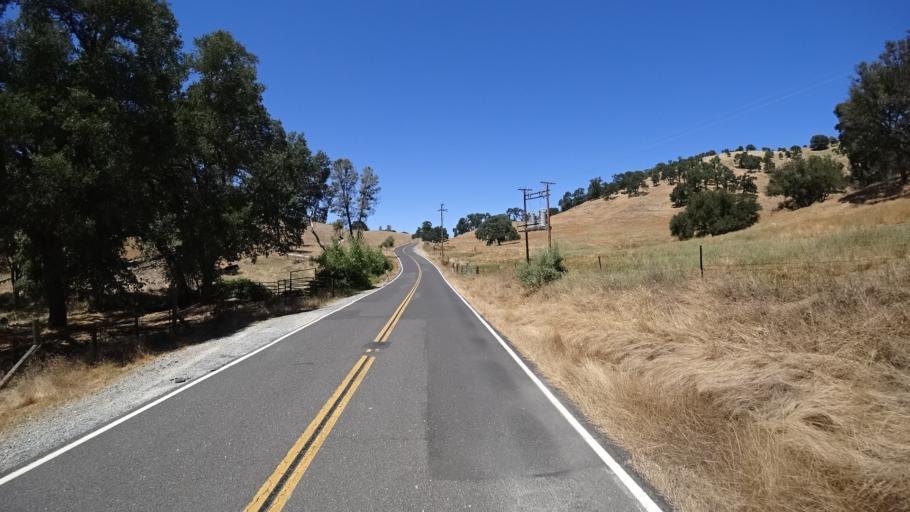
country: US
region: California
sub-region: Calaveras County
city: San Andreas
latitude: 38.1471
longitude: -120.6599
